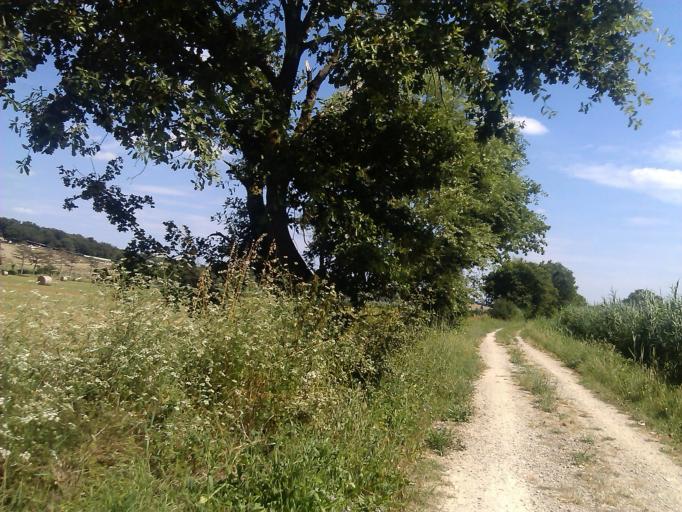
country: IT
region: Tuscany
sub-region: Provincia di Siena
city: Chiusi
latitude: 43.0697
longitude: 11.9277
